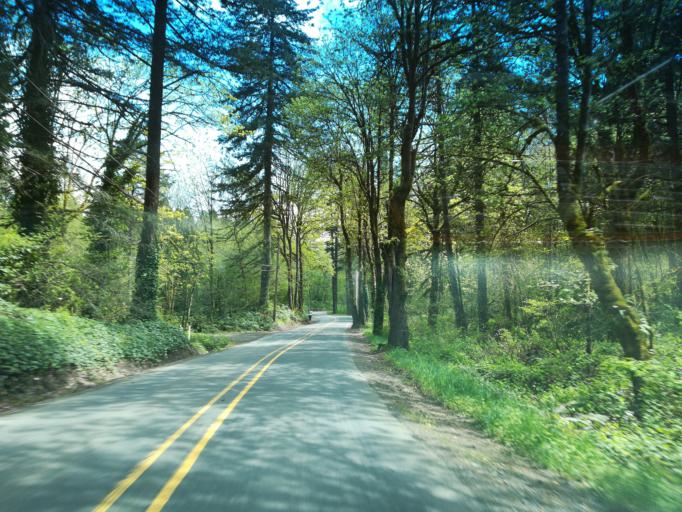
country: US
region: Oregon
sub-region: Clackamas County
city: Damascus
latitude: 45.4502
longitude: -122.4436
